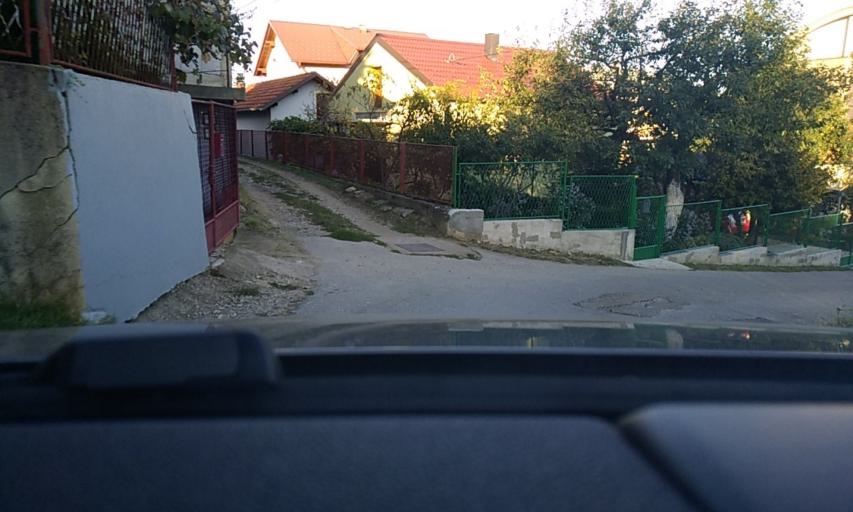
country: BA
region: Republika Srpska
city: Banja Luka
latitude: 44.7818
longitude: 17.1888
